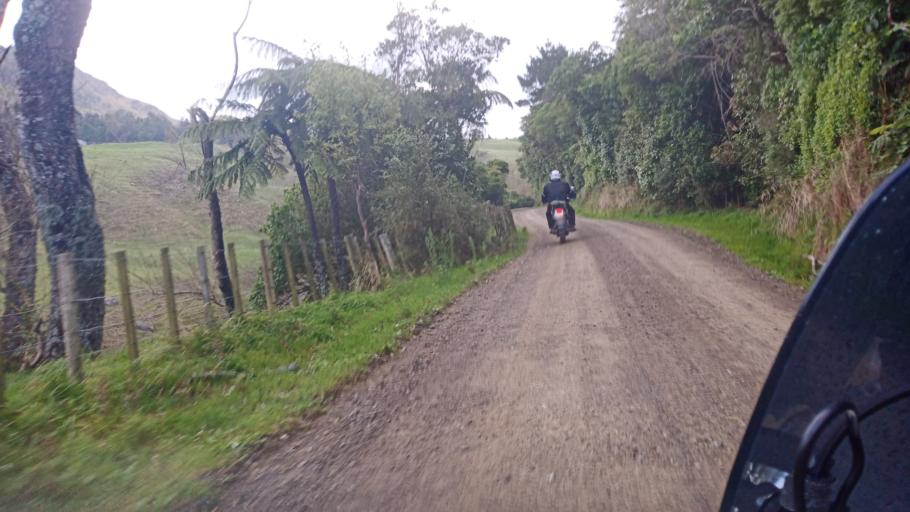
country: NZ
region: Gisborne
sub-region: Gisborne District
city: Gisborne
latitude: -38.4811
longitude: 177.6113
